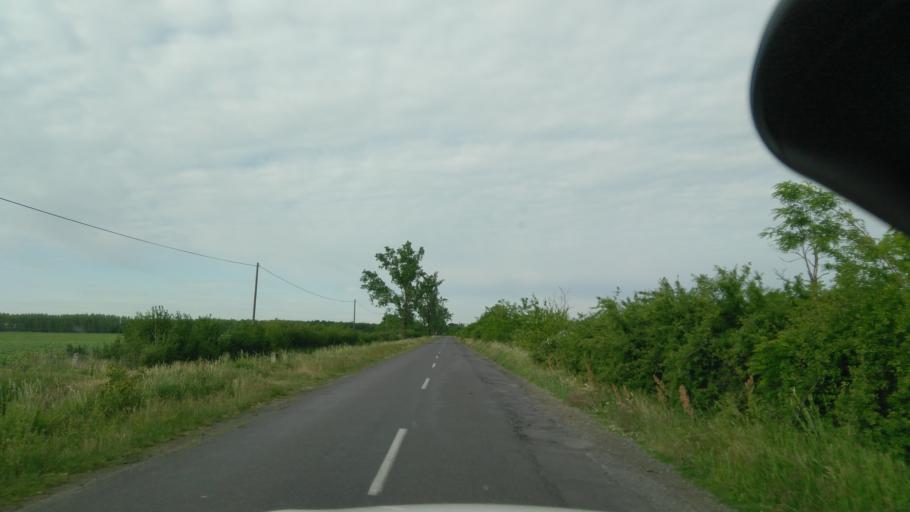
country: HU
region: Bekes
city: Elek
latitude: 46.5972
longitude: 21.2337
